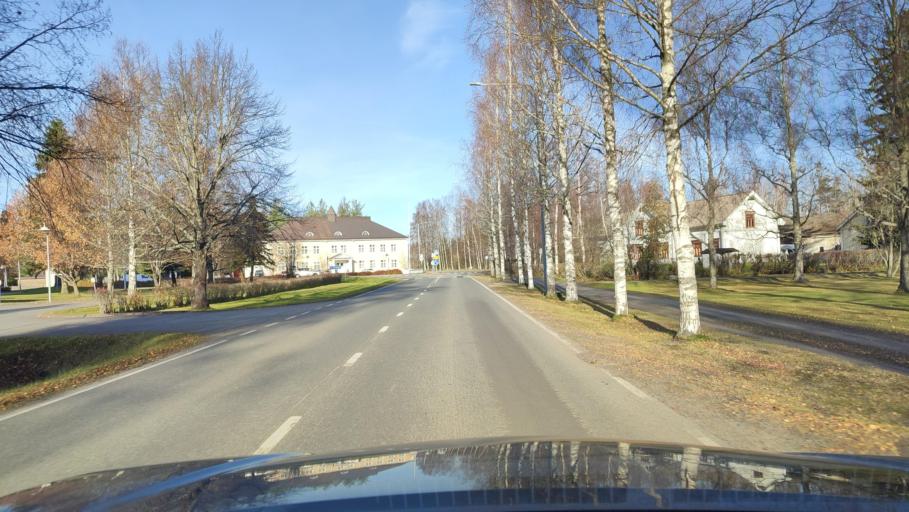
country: FI
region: Southern Ostrobothnia
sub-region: Suupohja
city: Teuva
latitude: 62.4785
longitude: 21.7398
